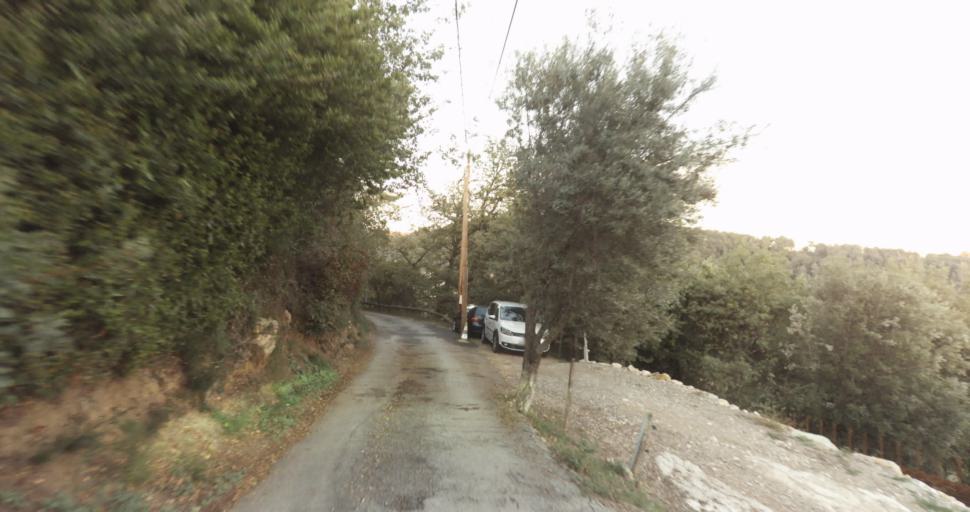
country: FR
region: Provence-Alpes-Cote d'Azur
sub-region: Departement des Alpes-Maritimes
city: La Gaude
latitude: 43.7215
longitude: 7.1361
